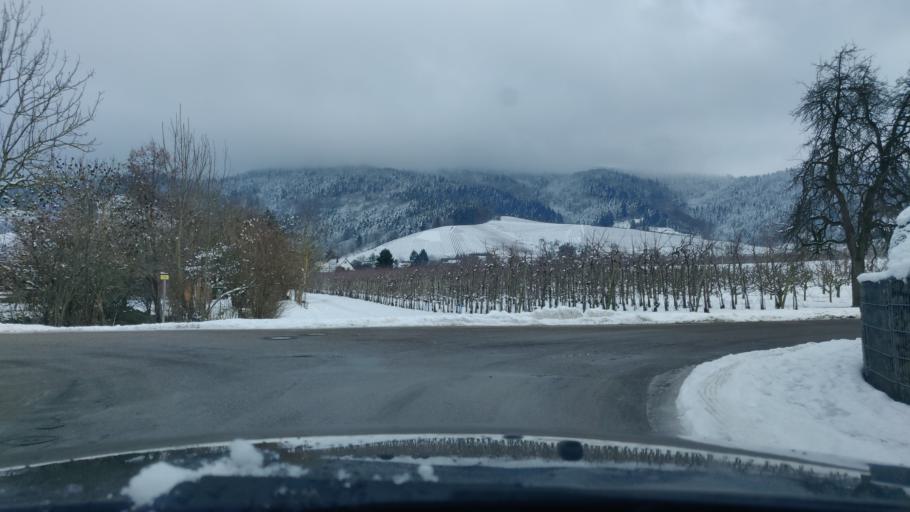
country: DE
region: Baden-Wuerttemberg
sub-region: Freiburg Region
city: Oberkirch
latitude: 48.5423
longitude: 8.0745
